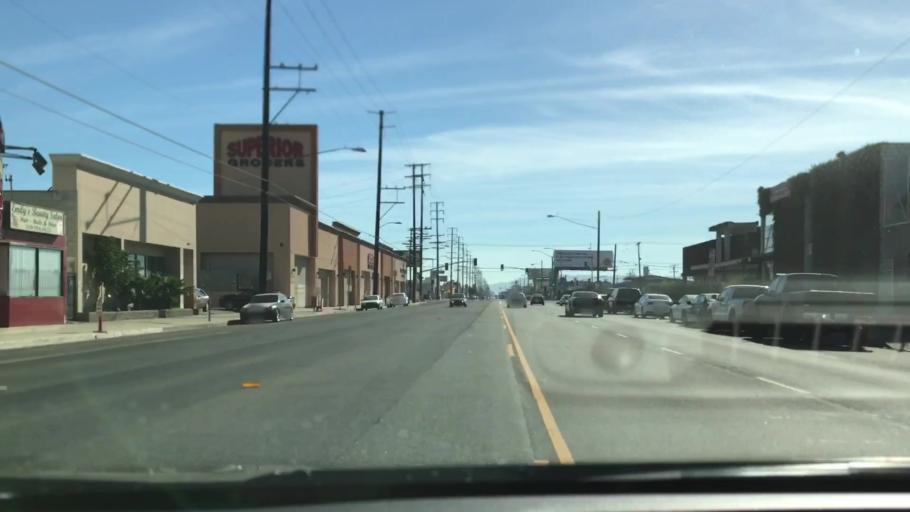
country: US
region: California
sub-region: Los Angeles County
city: Alondra Park
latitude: 33.8962
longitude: -118.3265
